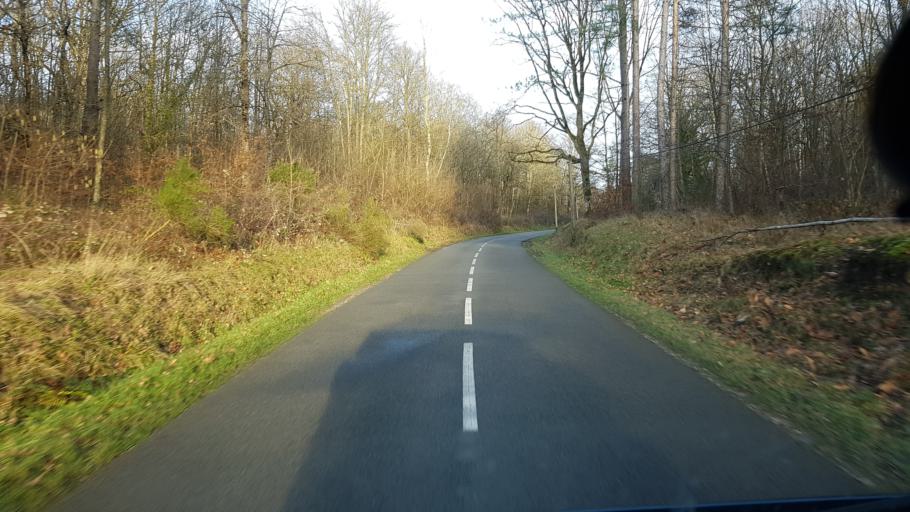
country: FR
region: Ile-de-France
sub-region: Departement des Yvelines
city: Saint-Leger-en-Yvelines
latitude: 48.6894
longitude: 1.7765
